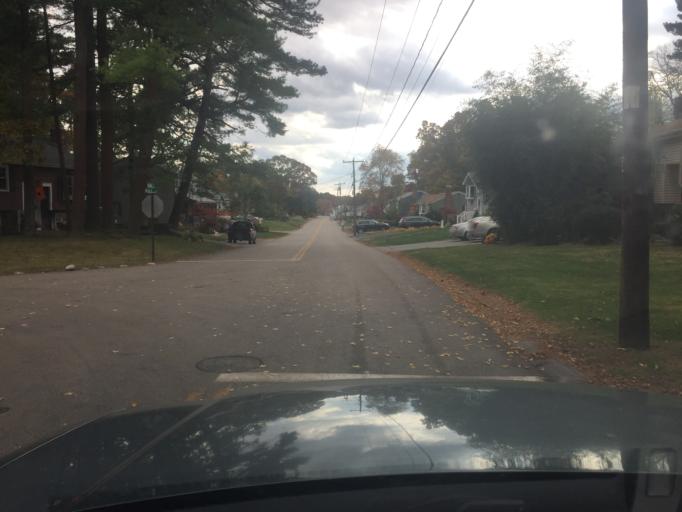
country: US
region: Massachusetts
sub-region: Norfolk County
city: Bellingham
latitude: 42.1093
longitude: -71.4832
